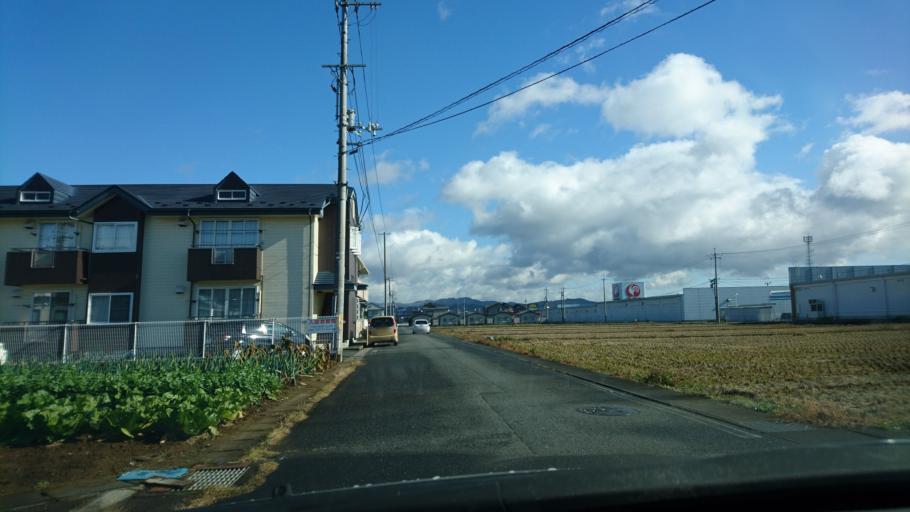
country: JP
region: Iwate
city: Ichinoseki
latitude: 38.9401
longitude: 141.1331
